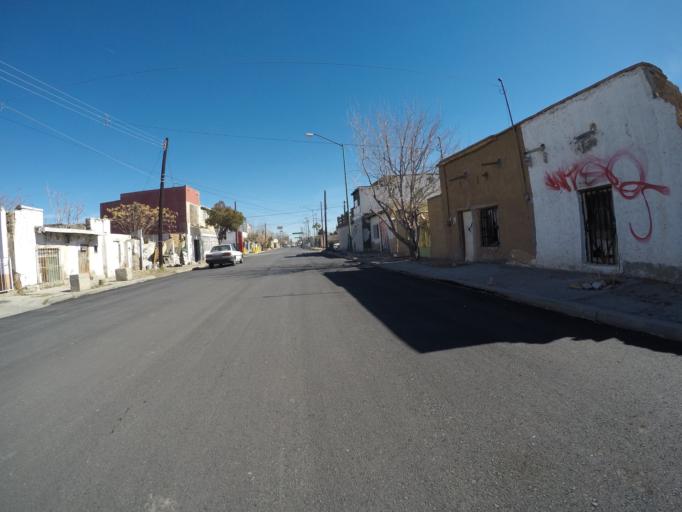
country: MX
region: Chihuahua
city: Ciudad Juarez
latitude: 31.7406
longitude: -106.4664
